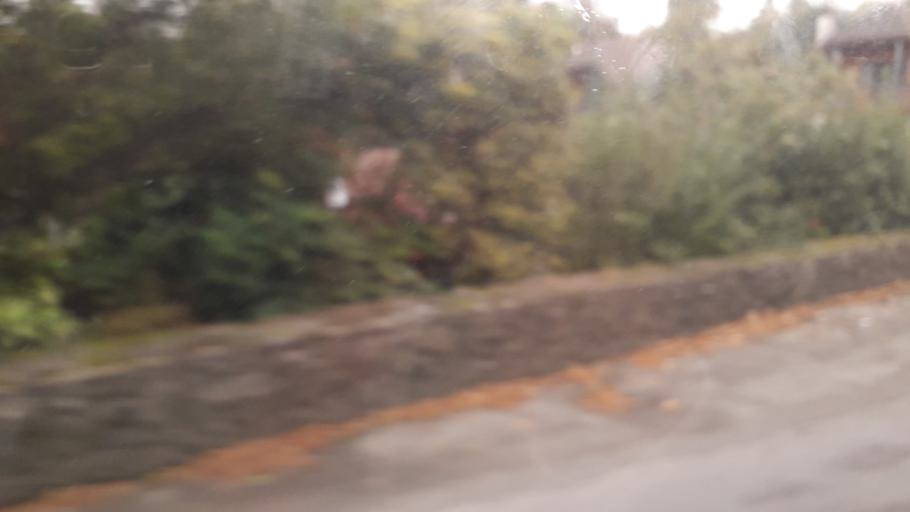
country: IE
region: Munster
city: Ballina
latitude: 52.8027
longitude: -8.4344
